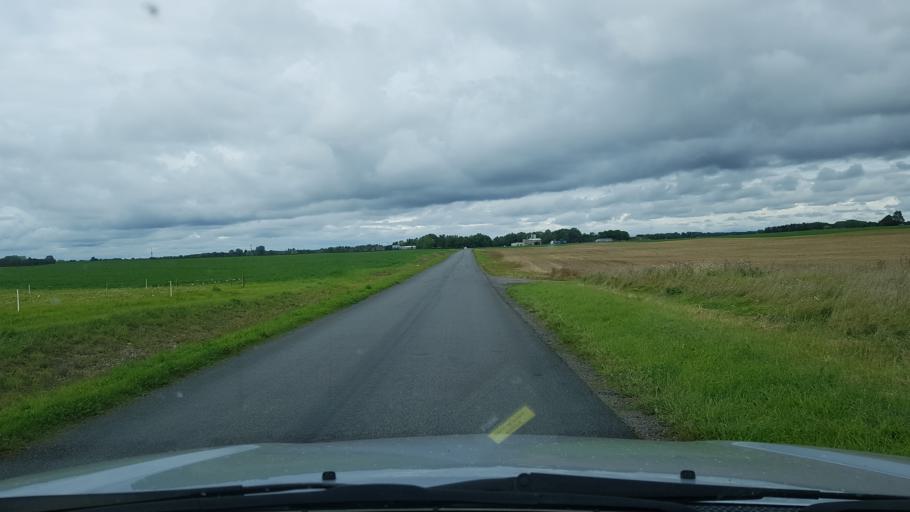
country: EE
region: Harju
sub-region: Rae vald
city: Vaida
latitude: 59.3541
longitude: 24.9643
